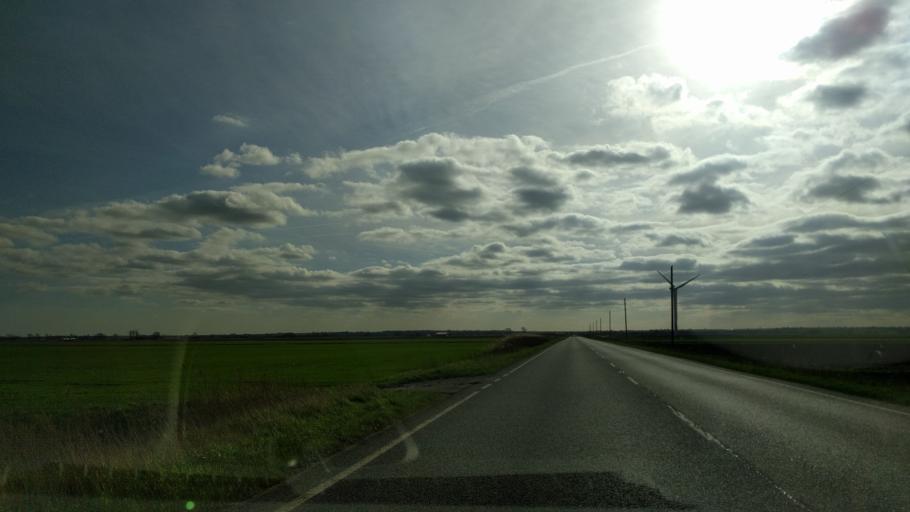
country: GB
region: England
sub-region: Cambridgeshire
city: Somersham
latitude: 52.4321
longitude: -0.0115
